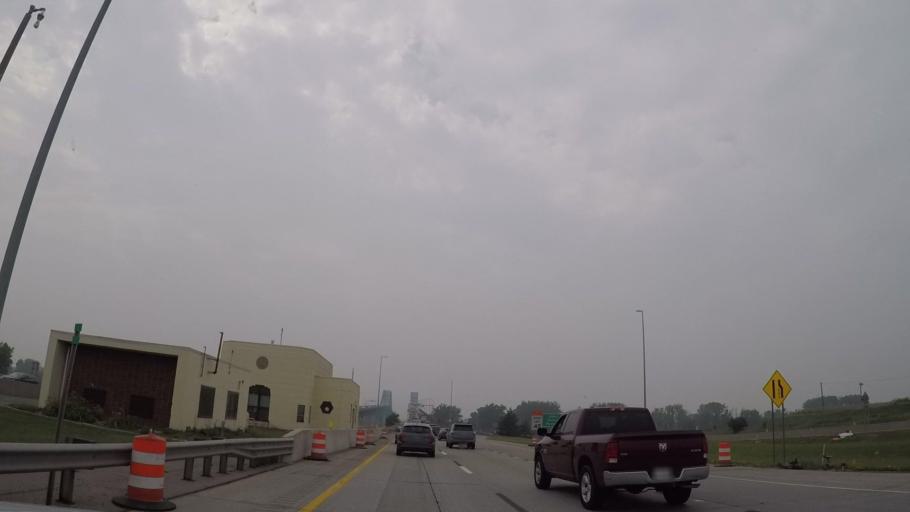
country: US
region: New York
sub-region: Erie County
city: Grandyle Village
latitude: 42.9939
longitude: -78.9297
